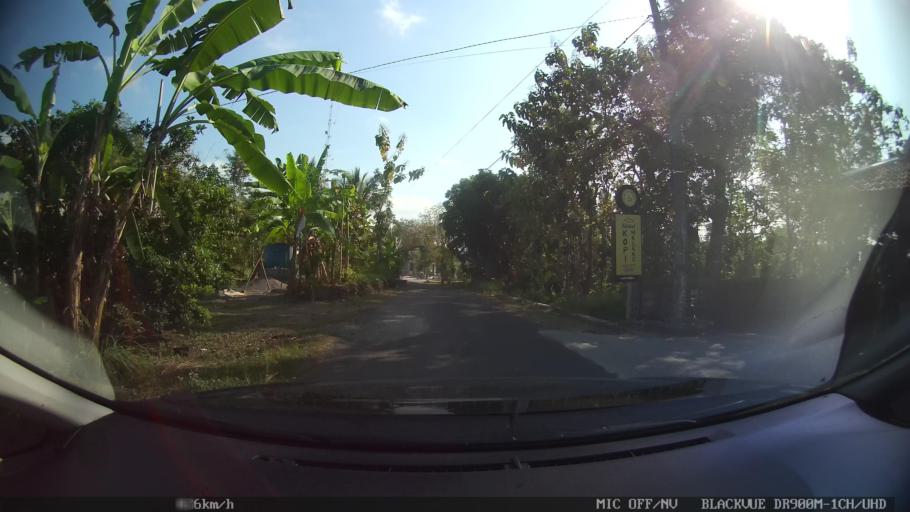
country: ID
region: Daerah Istimewa Yogyakarta
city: Kasihan
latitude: -7.8320
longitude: 110.2872
